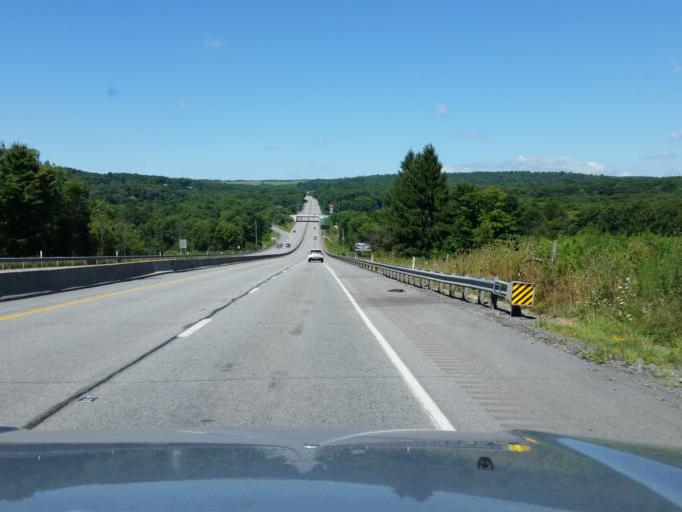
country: US
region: Pennsylvania
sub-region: Cambria County
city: Mundys Corner
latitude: 40.4491
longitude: -78.8293
